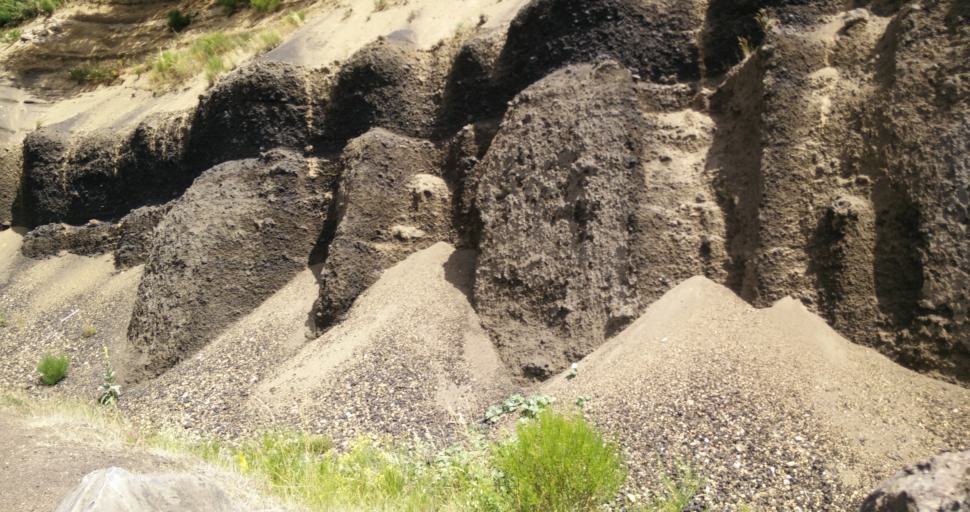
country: FR
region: Auvergne
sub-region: Departement du Puy-de-Dome
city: Saint-Ours
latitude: 45.8185
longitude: 2.9490
